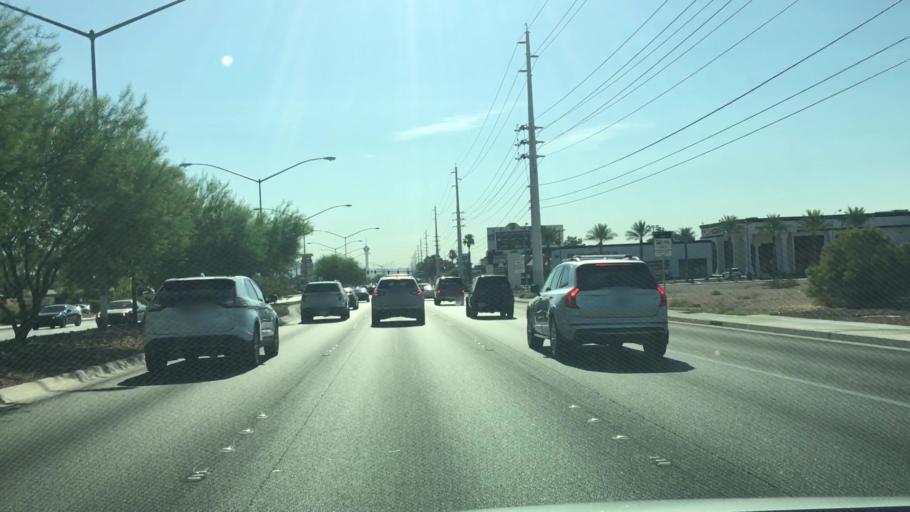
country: US
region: Nevada
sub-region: Clark County
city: Spring Valley
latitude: 36.1441
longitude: -115.2288
